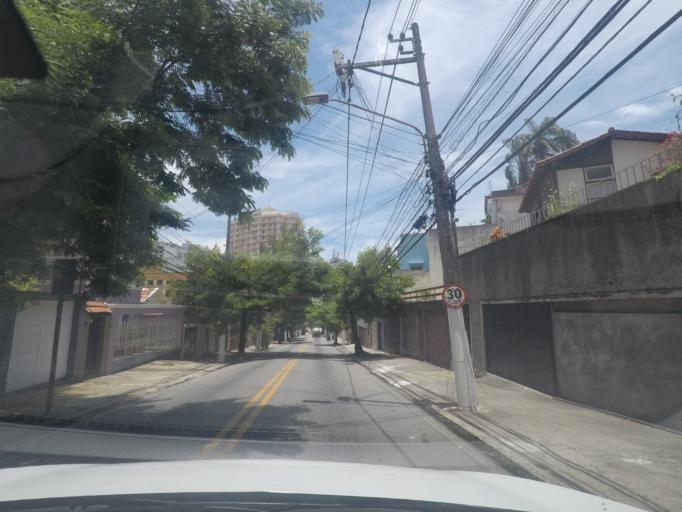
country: BR
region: Rio de Janeiro
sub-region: Niteroi
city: Niteroi
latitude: -22.9007
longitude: -43.1204
